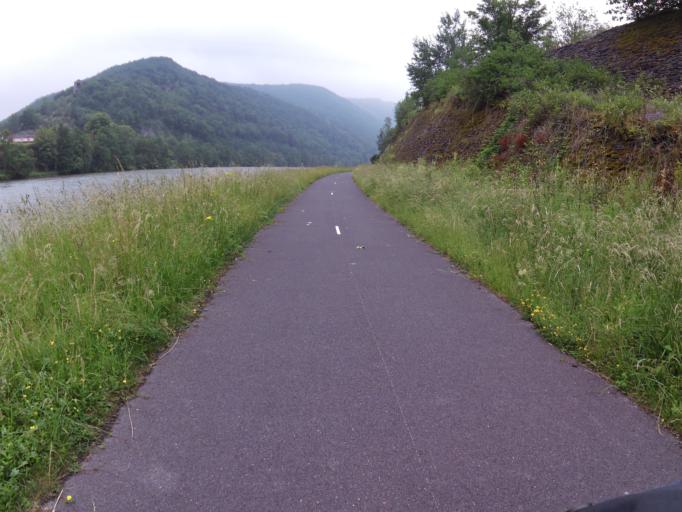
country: FR
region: Champagne-Ardenne
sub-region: Departement des Ardennes
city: Fumay
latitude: 49.9947
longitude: 4.6991
